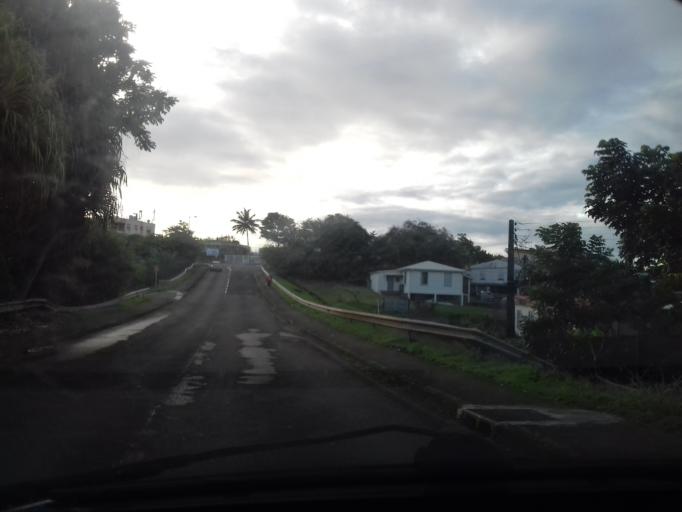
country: MQ
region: Martinique
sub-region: Martinique
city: Fort-de-France
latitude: 14.6167
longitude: -61.0855
